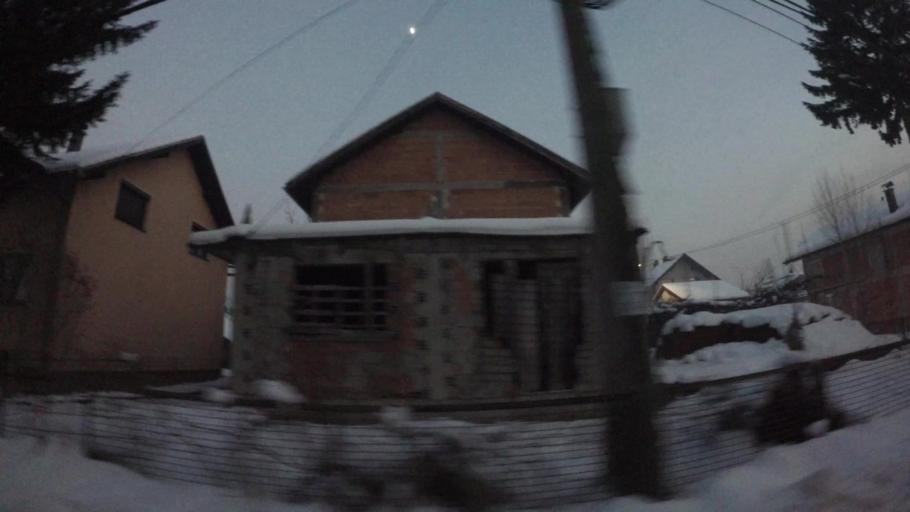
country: BA
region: Federation of Bosnia and Herzegovina
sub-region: Kanton Sarajevo
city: Sarajevo
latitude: 43.8337
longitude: 18.3203
